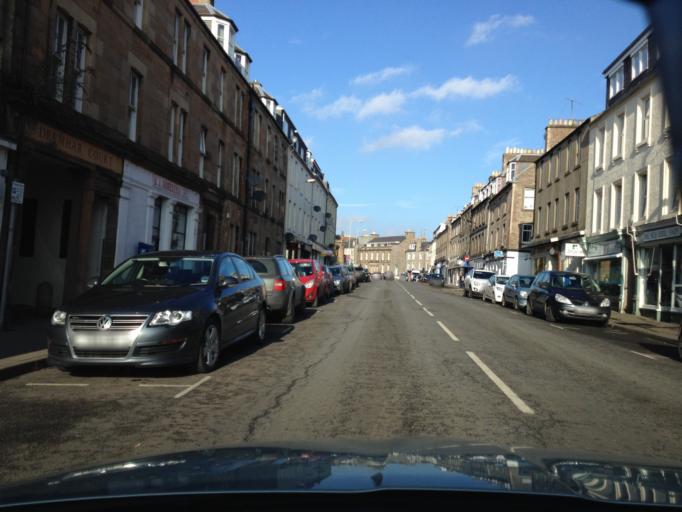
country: GB
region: Scotland
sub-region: Perth and Kinross
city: Perth
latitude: 56.3978
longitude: -3.4346
